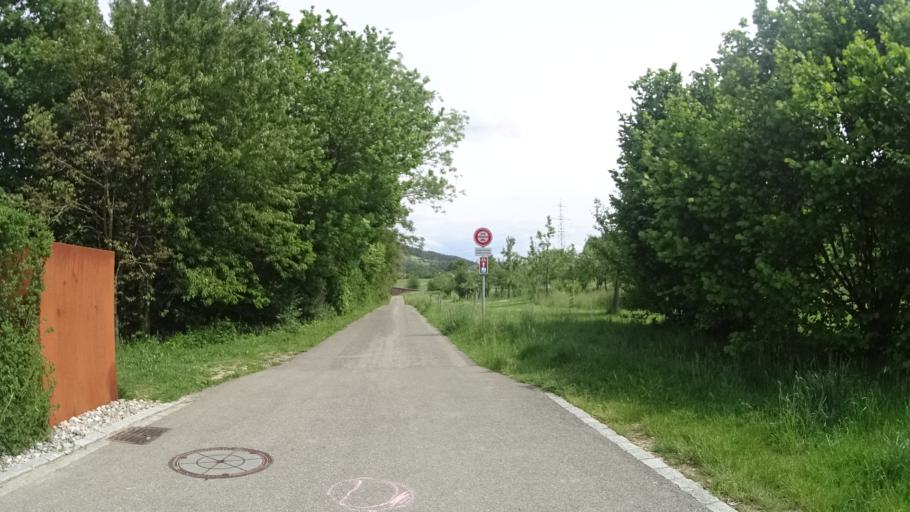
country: CH
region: Aargau
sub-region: Bezirk Rheinfelden
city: Mohlin
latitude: 47.5494
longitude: 7.8559
